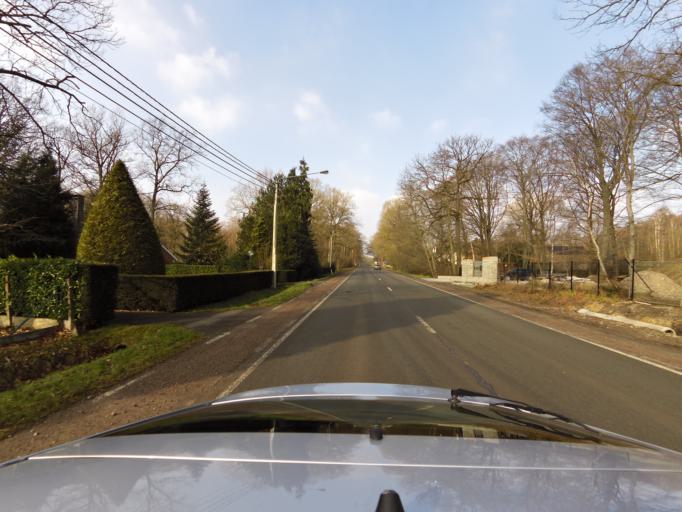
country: BE
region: Wallonia
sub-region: Province du Hainaut
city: Beloeil
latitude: 50.4882
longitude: 3.7333
